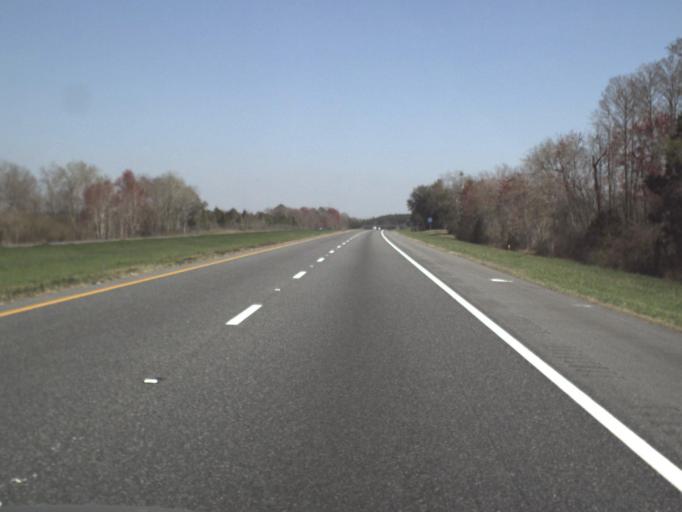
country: US
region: Florida
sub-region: Washington County
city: Chipley
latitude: 30.7466
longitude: -85.4297
